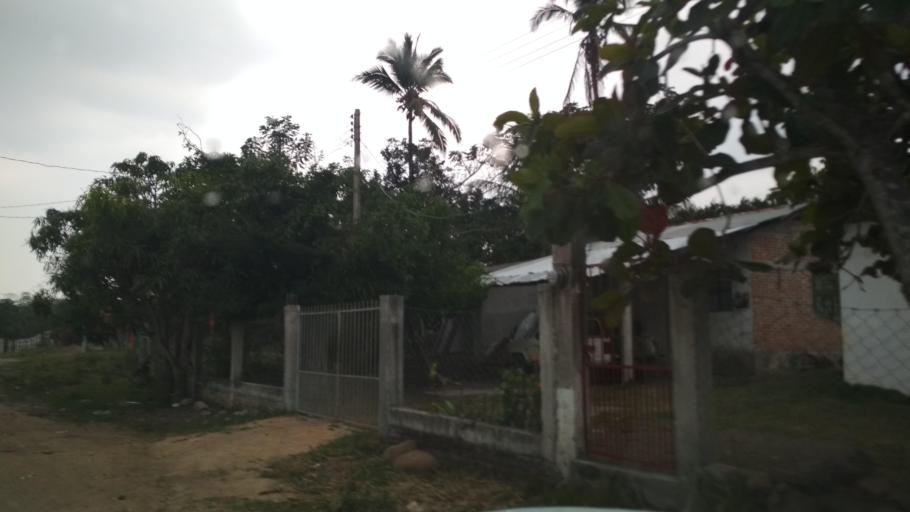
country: MM
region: Shan
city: Taunggyi
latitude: 20.3335
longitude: 97.3102
